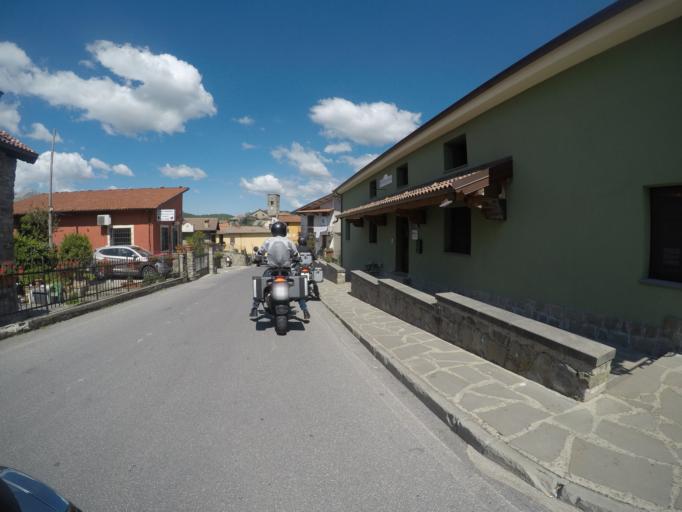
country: IT
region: Tuscany
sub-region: Provincia di Lucca
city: Careggine
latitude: 44.1201
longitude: 10.3258
